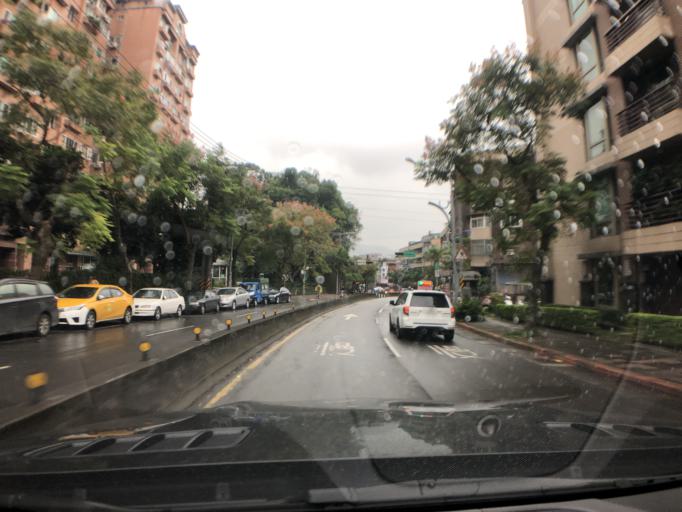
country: TW
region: Taipei
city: Taipei
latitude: 24.9894
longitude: 121.5524
